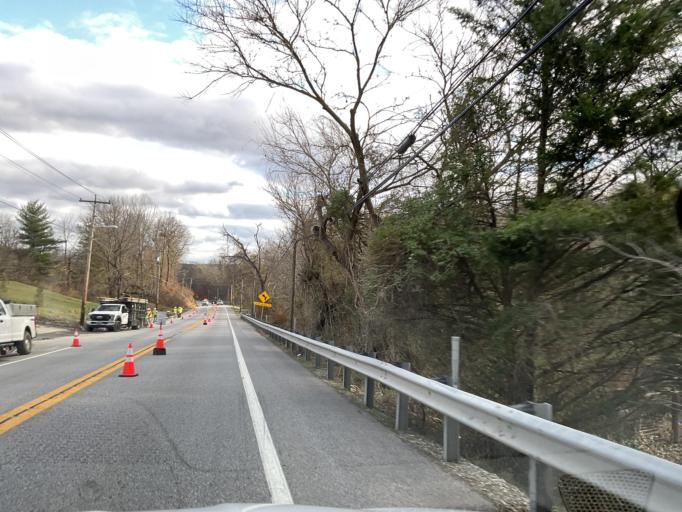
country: US
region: Pennsylvania
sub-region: Adams County
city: Mount Pleasant
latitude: 39.6765
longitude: -77.0361
